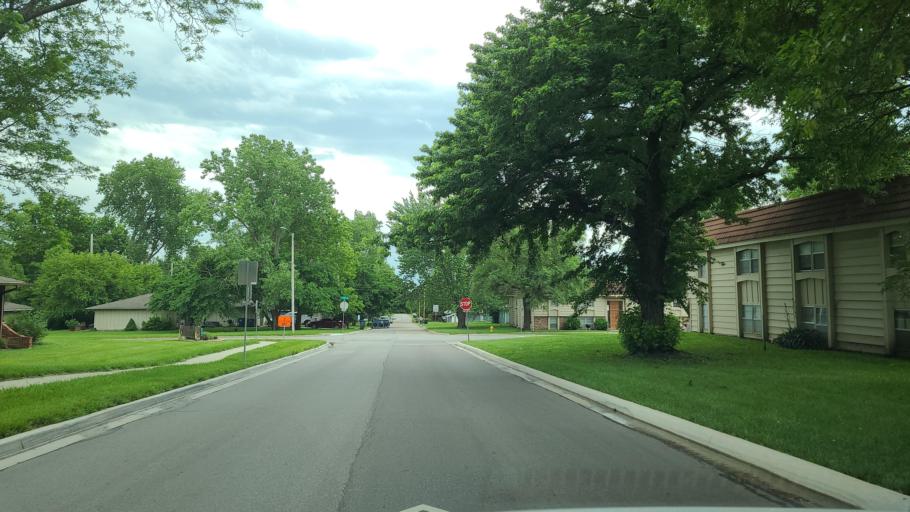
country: US
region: Kansas
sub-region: Douglas County
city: Lawrence
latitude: 38.9350
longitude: -95.2579
